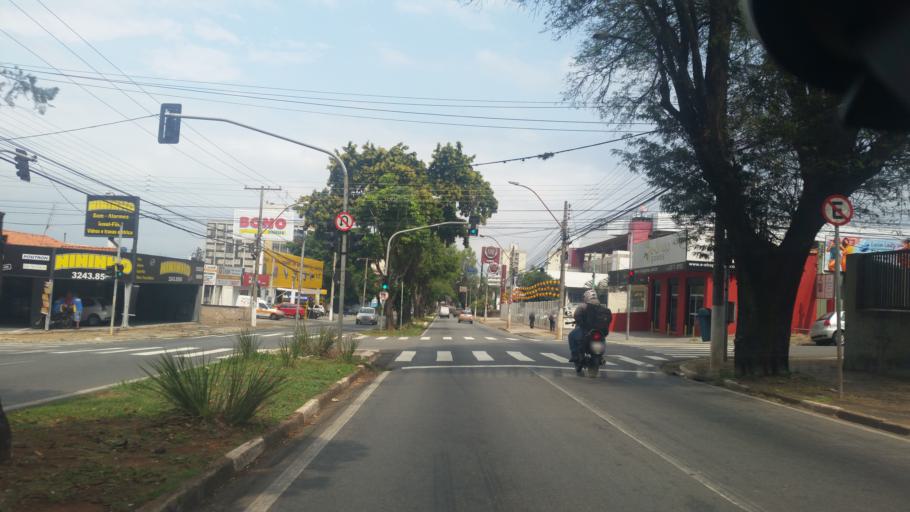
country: BR
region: Sao Paulo
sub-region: Campinas
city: Campinas
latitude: -22.8972
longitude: -47.0804
